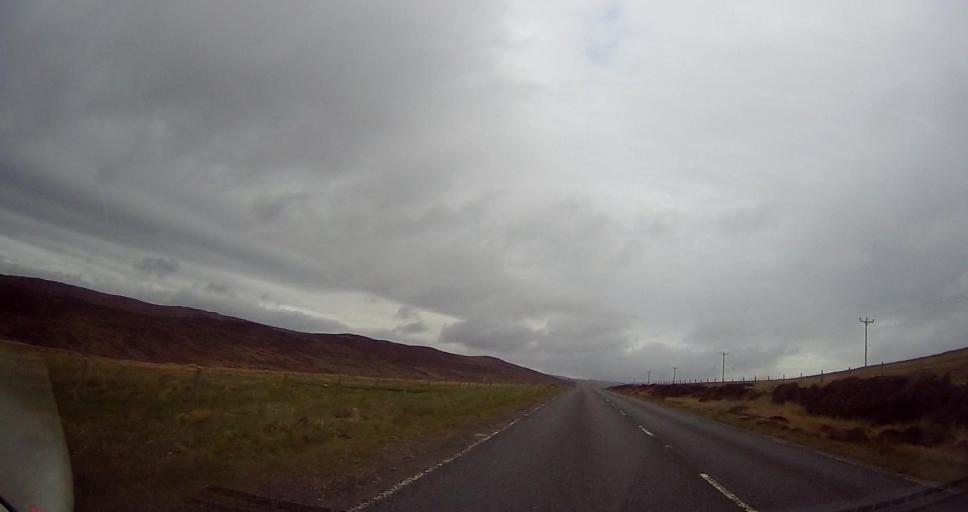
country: GB
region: Scotland
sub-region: Shetland Islands
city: Lerwick
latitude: 60.2021
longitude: -1.2331
